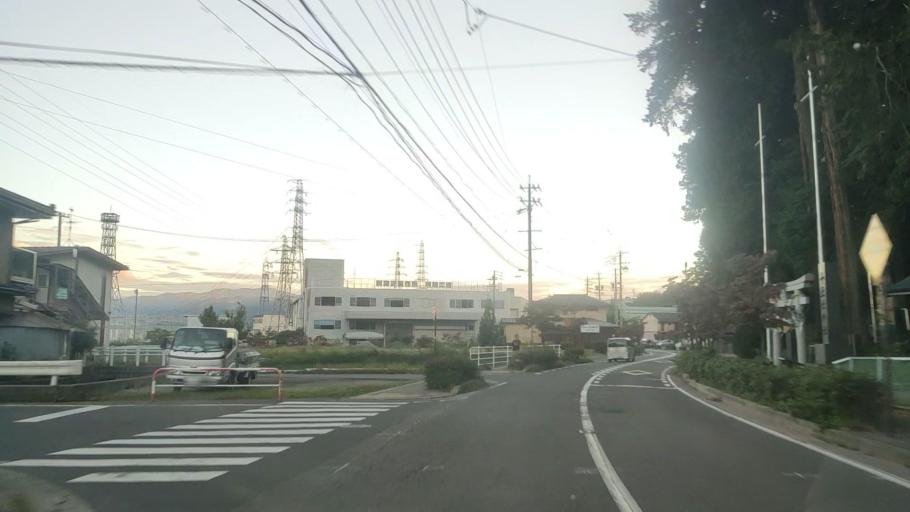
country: JP
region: Nagano
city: Okaya
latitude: 36.0792
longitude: 138.0432
